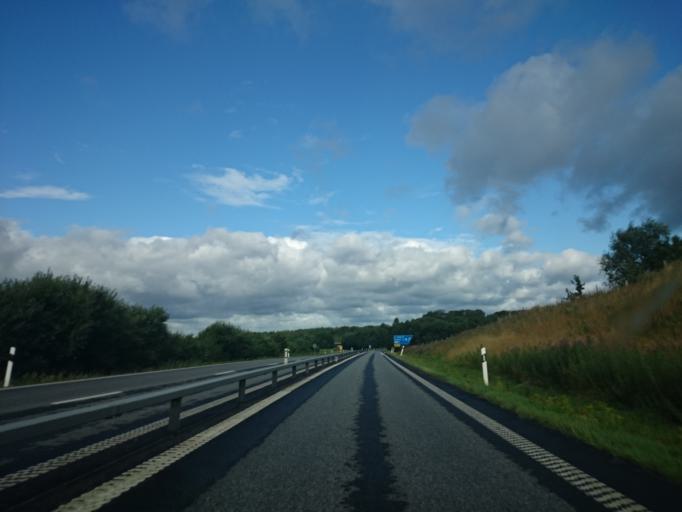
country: SE
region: Skane
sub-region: Horby Kommun
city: Hoerby
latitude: 55.8647
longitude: 13.6713
